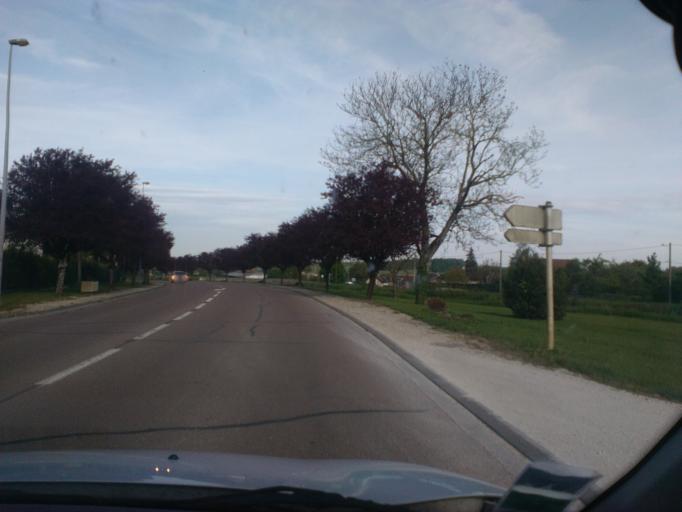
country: FR
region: Champagne-Ardenne
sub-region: Departement de l'Aube
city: Vendeuvre-sur-Barse
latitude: 48.2403
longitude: 4.4723
